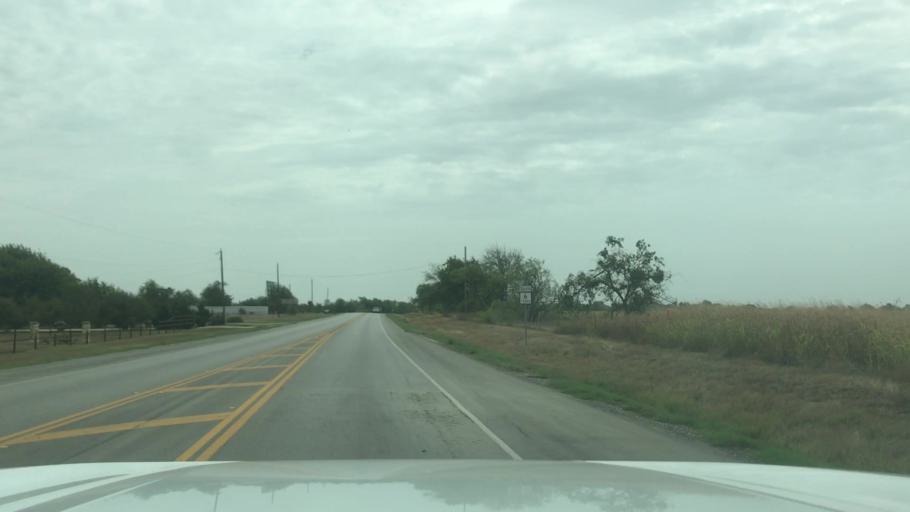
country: US
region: Texas
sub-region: Erath County
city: Dublin
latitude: 32.0928
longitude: -98.3670
